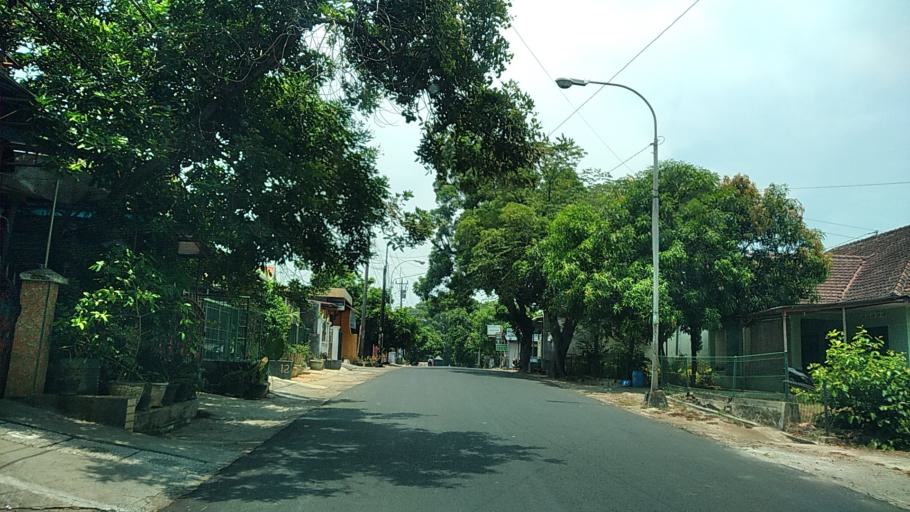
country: ID
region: Central Java
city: Semarang
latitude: -7.0566
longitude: 110.4138
